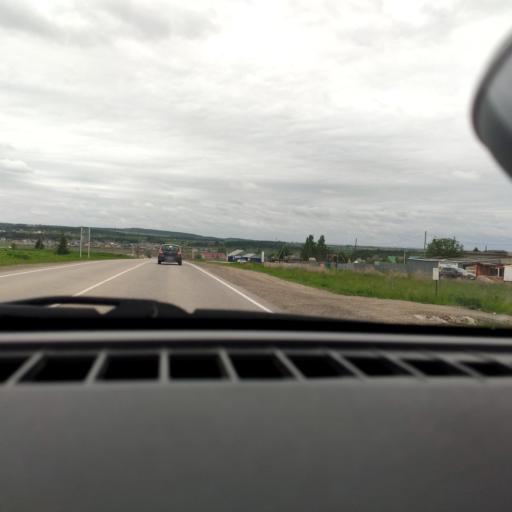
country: RU
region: Perm
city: Kultayevo
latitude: 57.8654
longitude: 55.8753
